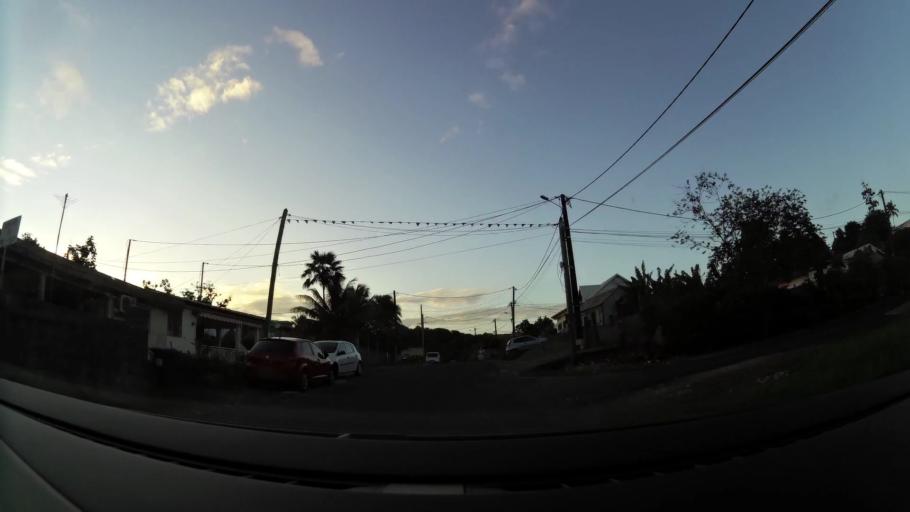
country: GP
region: Guadeloupe
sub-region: Guadeloupe
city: Les Abymes
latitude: 16.2695
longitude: -61.4964
